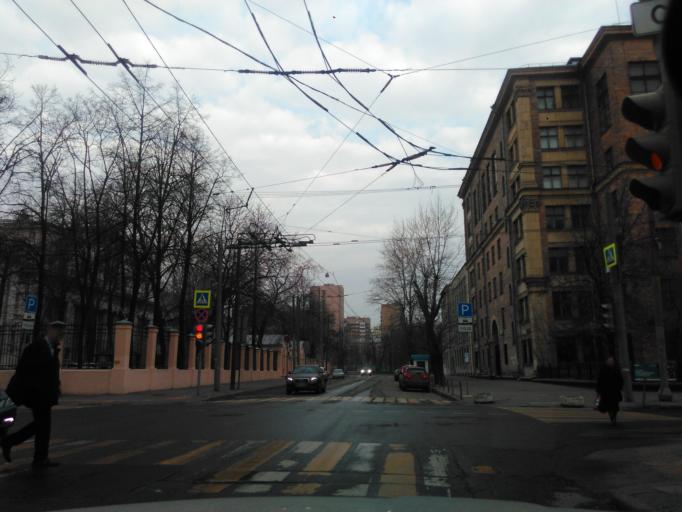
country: RU
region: Moscow
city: Moscow
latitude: 55.7761
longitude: 37.5959
